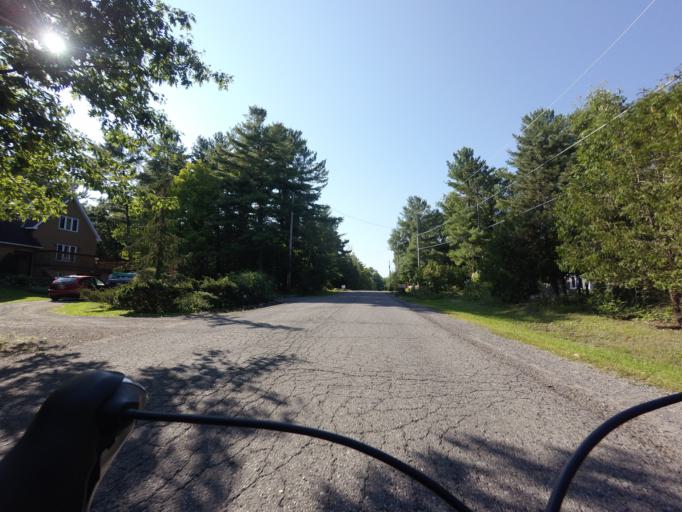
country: CA
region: Ontario
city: Bells Corners
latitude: 45.4868
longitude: -76.0421
